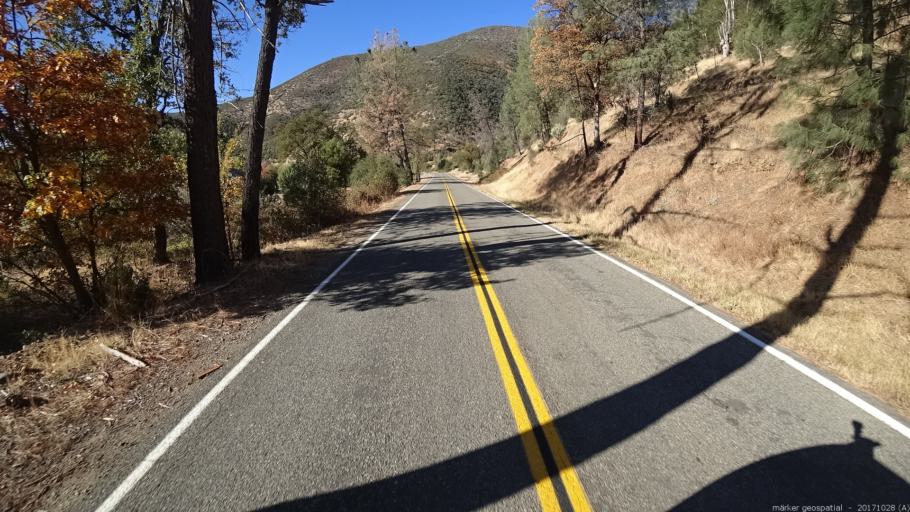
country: US
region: California
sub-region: Trinity County
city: Lewiston
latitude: 40.7177
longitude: -122.6331
